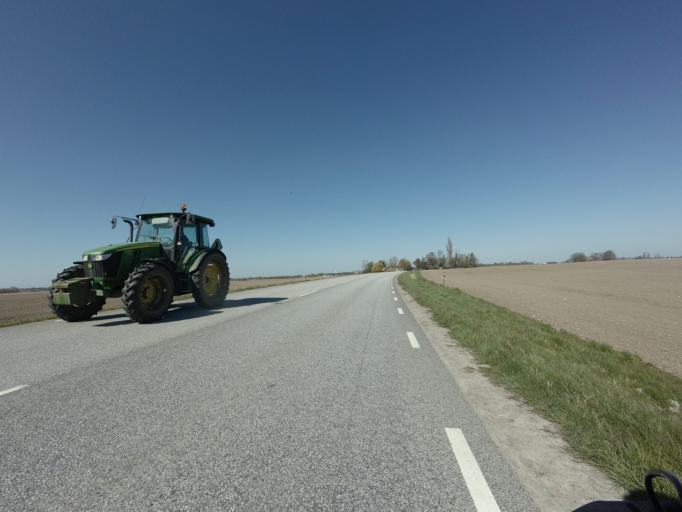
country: SE
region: Skane
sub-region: Vellinge Kommun
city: Vellinge
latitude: 55.4669
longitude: 13.0569
